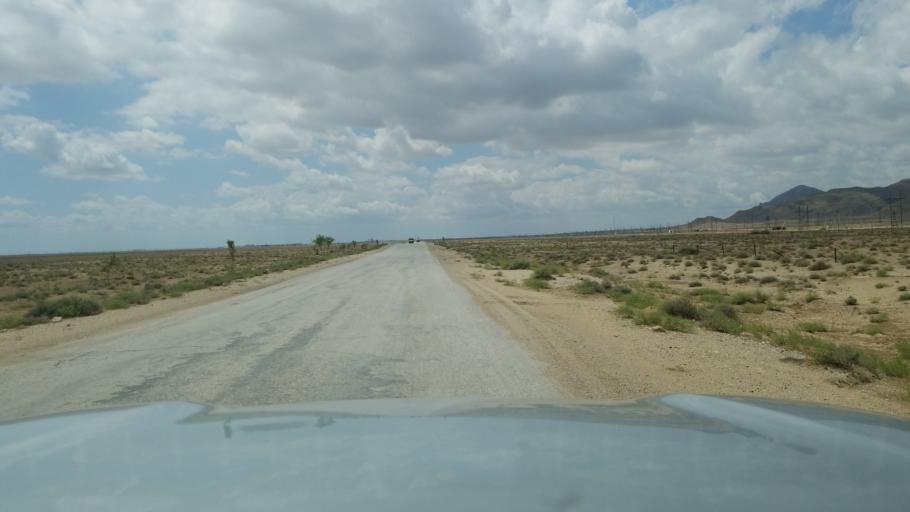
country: TM
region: Balkan
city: Balkanabat
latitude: 39.4809
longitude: 54.4509
